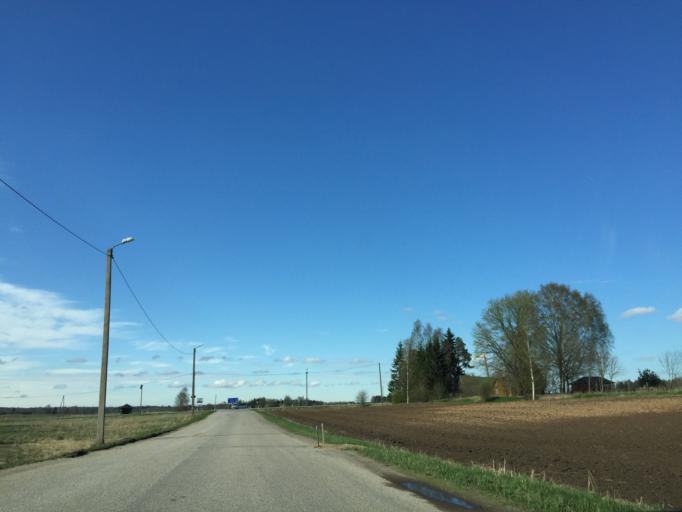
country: EE
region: Valgamaa
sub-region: Valga linn
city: Valga
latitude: 57.8693
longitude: 26.2510
